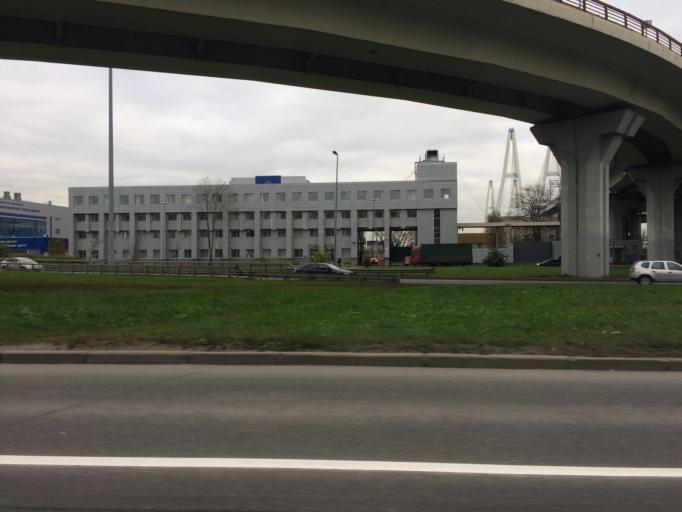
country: RU
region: Leningrad
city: Rybatskoye
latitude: 59.8541
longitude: 30.4792
